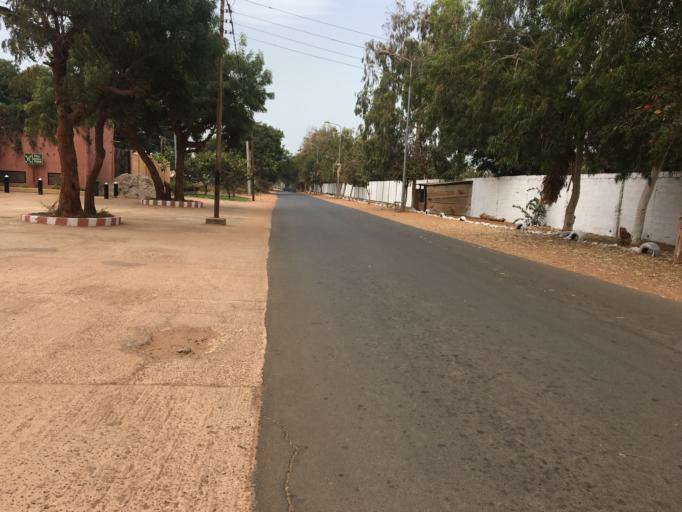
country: GM
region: Banjul
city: Bakau
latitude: 13.4785
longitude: -16.6827
